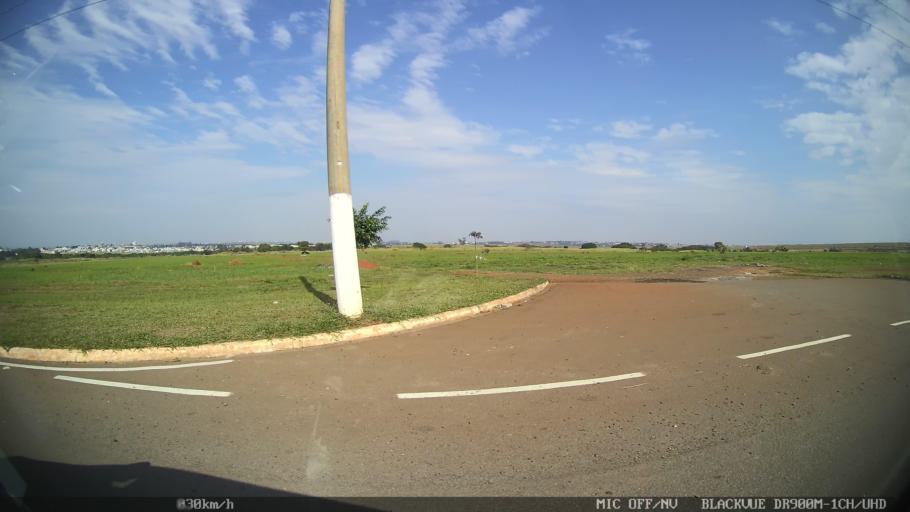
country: BR
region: Sao Paulo
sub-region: Paulinia
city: Paulinia
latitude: -22.7847
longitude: -47.1525
